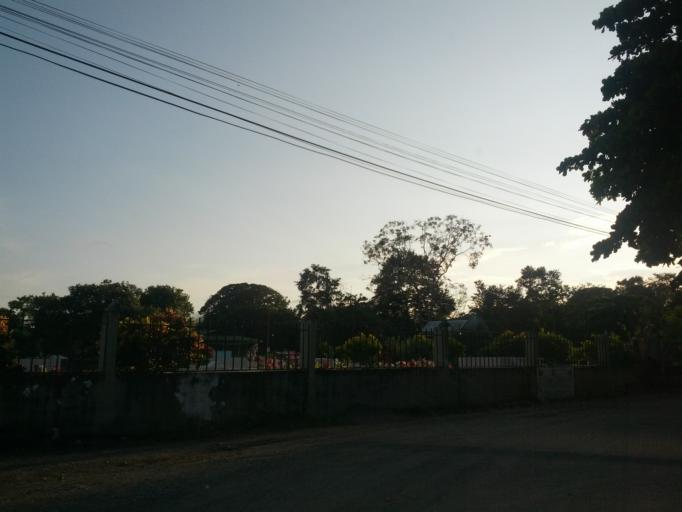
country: CR
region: Puntarenas
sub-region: Canton de Golfito
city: Golfito
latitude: 8.5362
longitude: -83.3015
